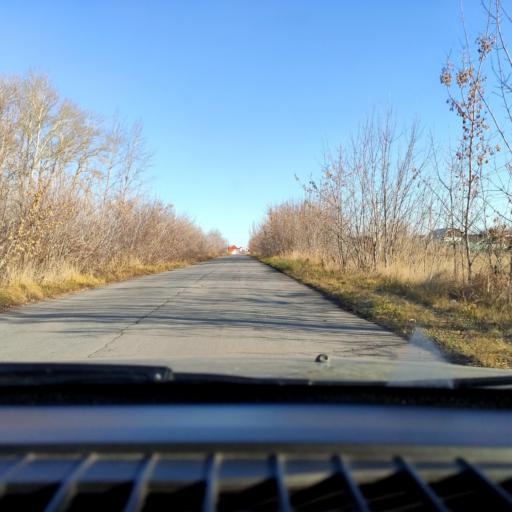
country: RU
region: Samara
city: Tol'yatti
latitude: 53.6622
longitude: 49.3351
